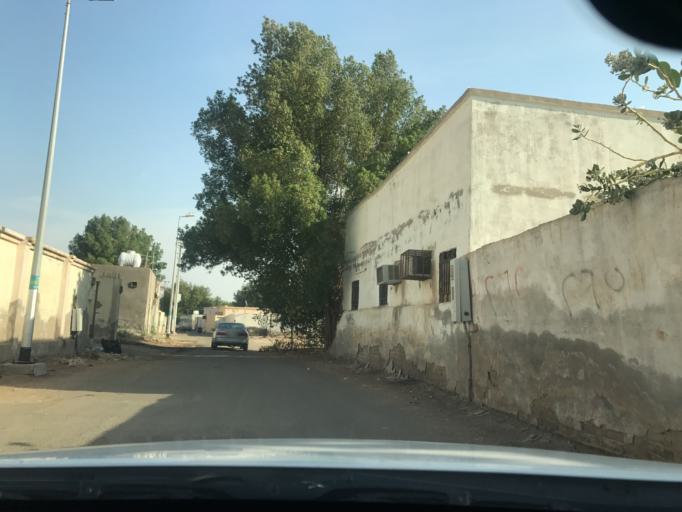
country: SA
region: Makkah
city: Al Jumum
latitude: 21.4480
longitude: 39.5330
